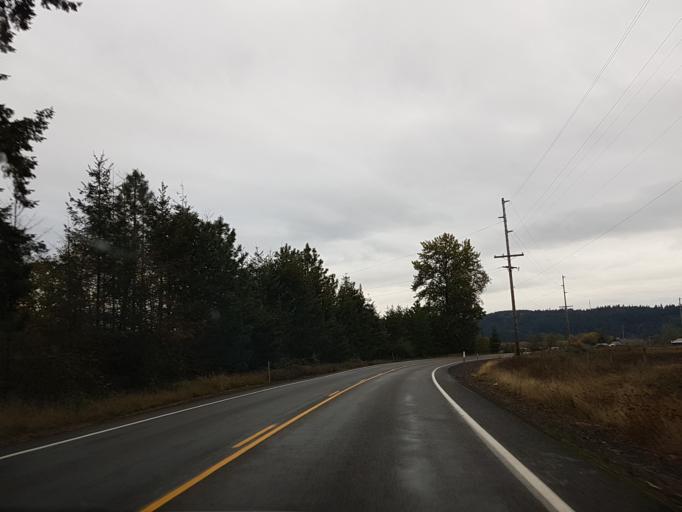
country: US
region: Oregon
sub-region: Marion County
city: Stayton
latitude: 44.7068
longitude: -122.7943
